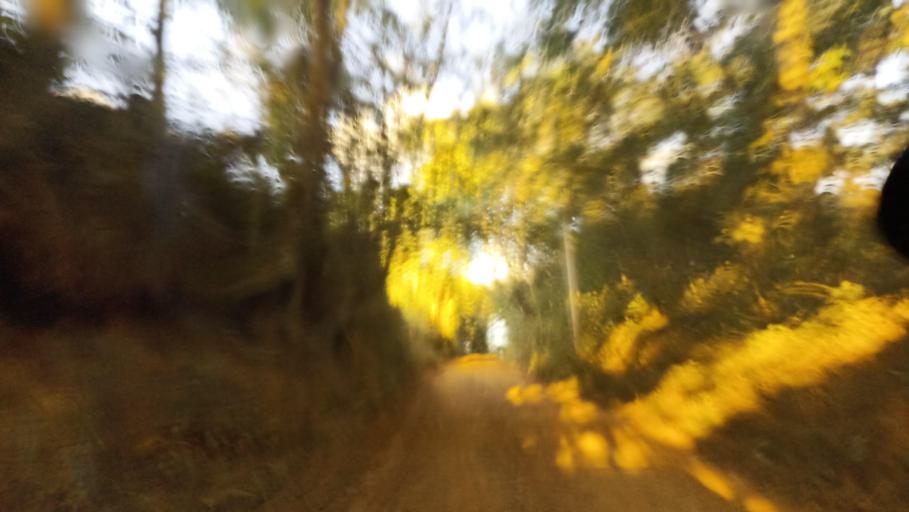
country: BR
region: Minas Gerais
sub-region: Sao Joao Del Rei
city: Sao Joao del Rei
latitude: -21.1836
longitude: -44.3477
